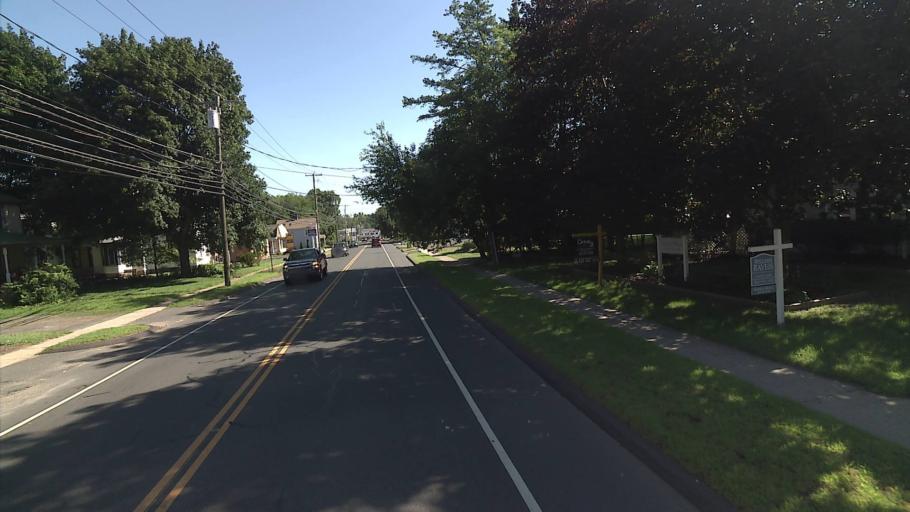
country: US
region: Connecticut
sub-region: New Haven County
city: Cheshire Village
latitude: 41.5845
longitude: -72.8922
